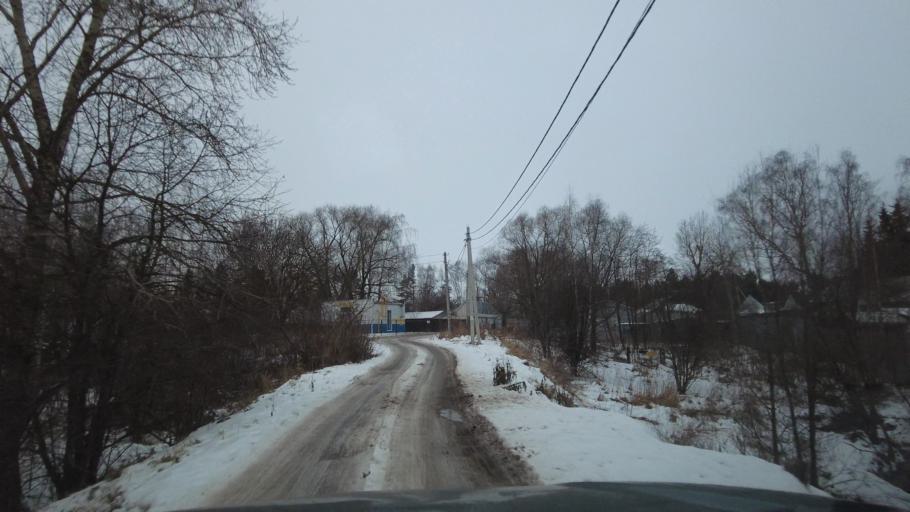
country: RU
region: Moskovskaya
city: Novopodrezkovo
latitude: 55.9762
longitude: 37.3813
